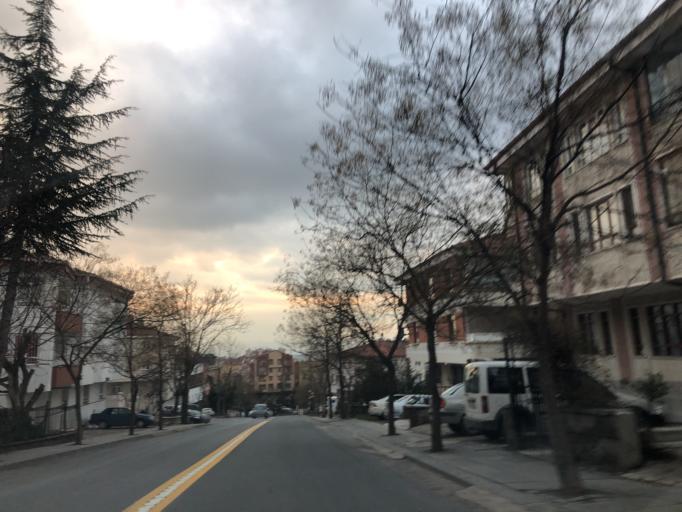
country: TR
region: Ankara
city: Ankara
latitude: 39.9756
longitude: 32.8182
